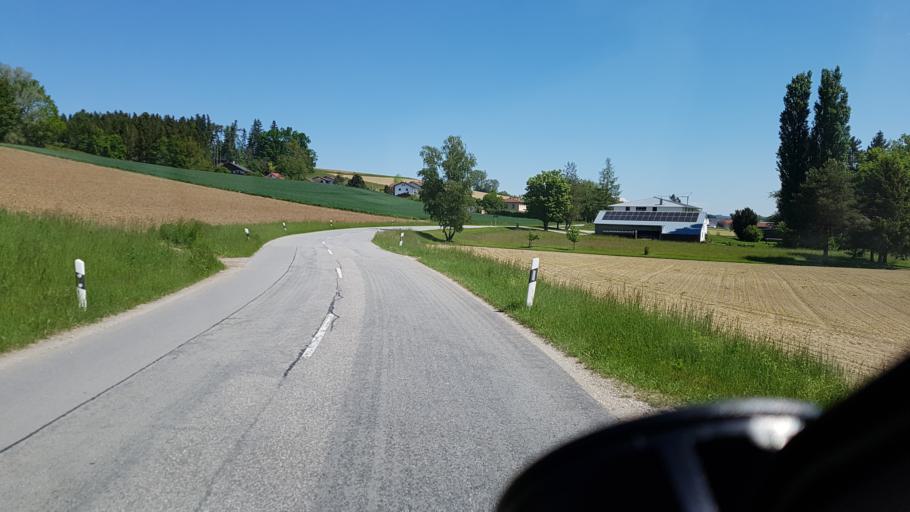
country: DE
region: Bavaria
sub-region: Lower Bavaria
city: Pfarrkirchen
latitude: 48.4071
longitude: 12.9393
